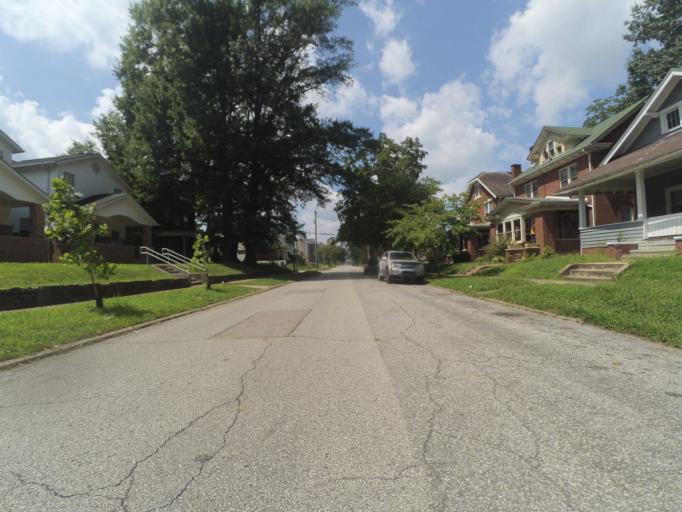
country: US
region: West Virginia
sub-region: Cabell County
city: Huntington
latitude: 38.4148
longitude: -82.4251
